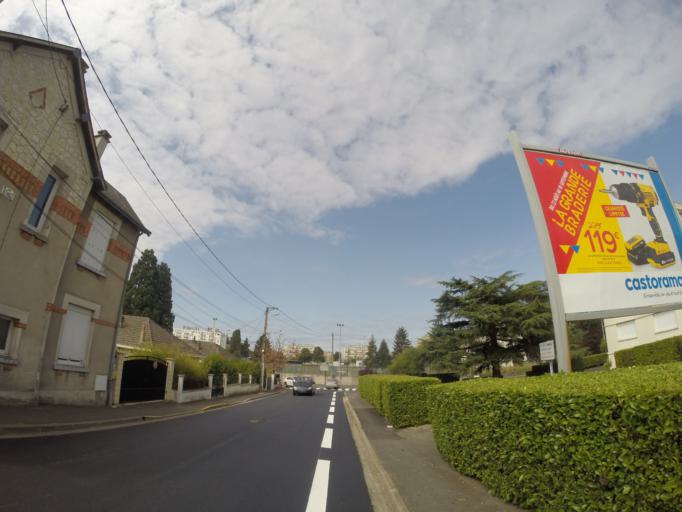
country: FR
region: Centre
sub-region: Departement d'Indre-et-Loire
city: Tours
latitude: 47.4123
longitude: 0.6976
